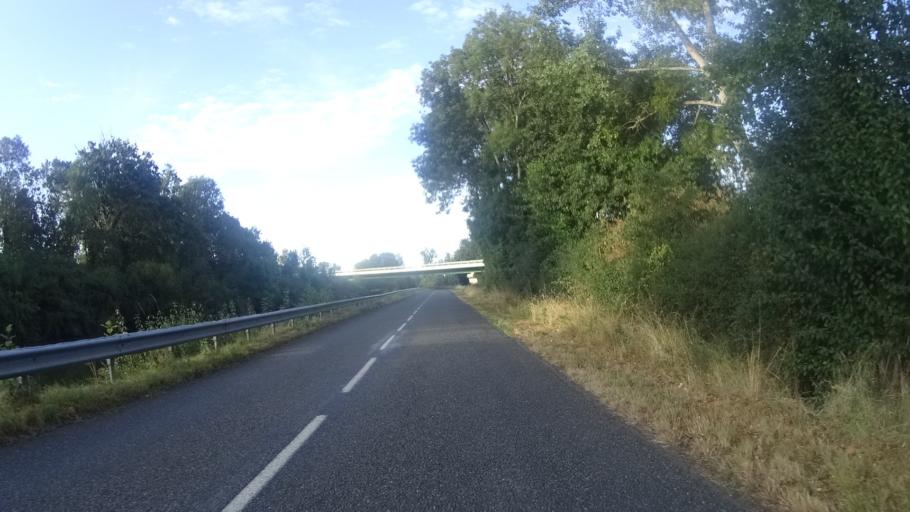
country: FR
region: Bourgogne
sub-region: Departement de Saone-et-Loire
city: Paray-le-Monial
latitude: 46.4588
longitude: 4.1590
